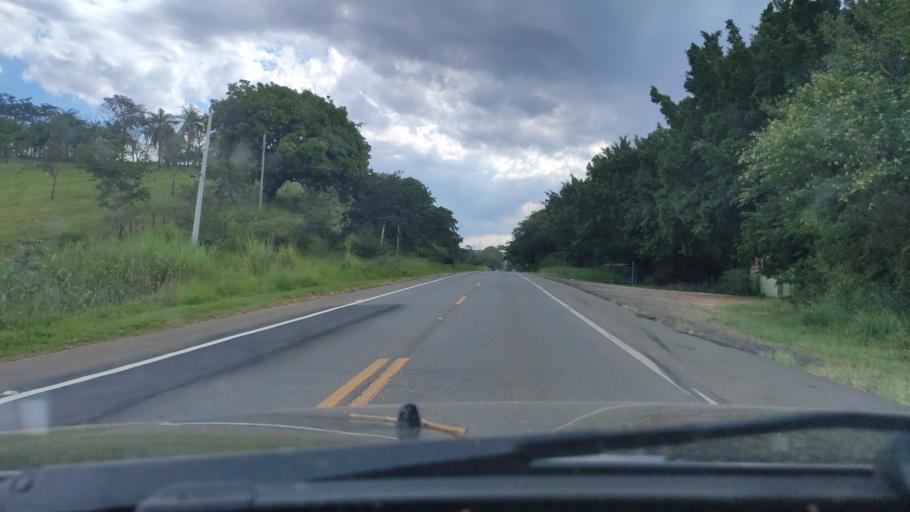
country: BR
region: Sao Paulo
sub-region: Aguas De Lindoia
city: Aguas de Lindoia
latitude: -22.4600
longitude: -46.7277
